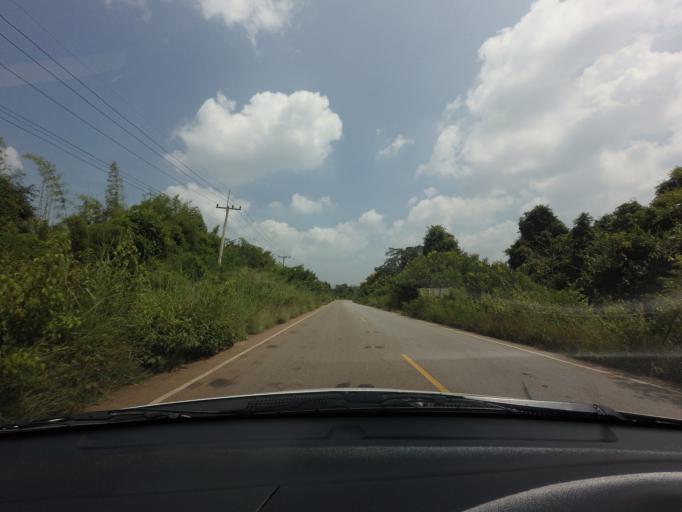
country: TH
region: Nakhon Ratchasima
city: Pak Chong
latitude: 14.5854
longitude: 101.5679
